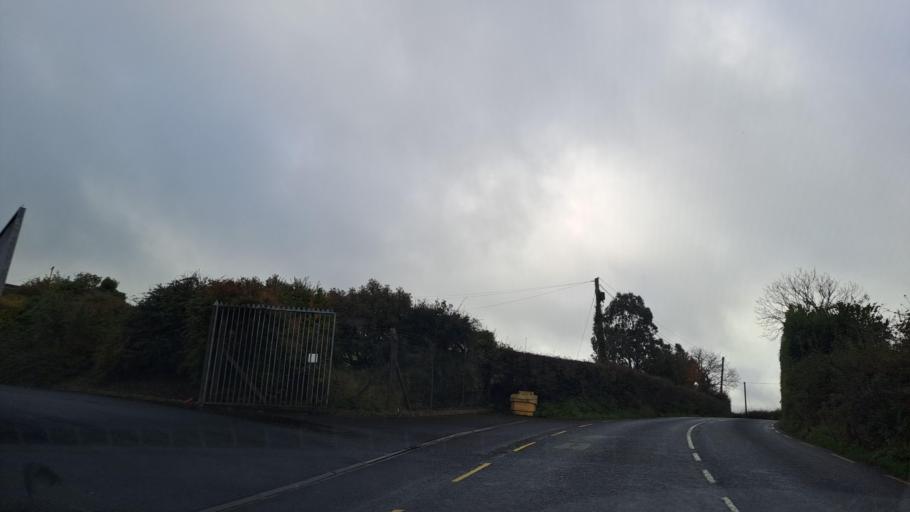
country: IE
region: Ulster
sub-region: An Cabhan
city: Bailieborough
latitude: 53.8945
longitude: -7.0140
